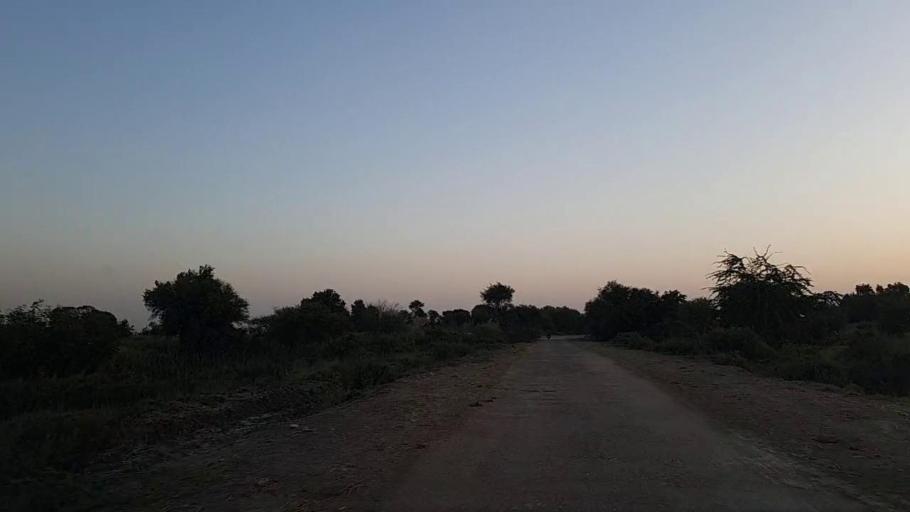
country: PK
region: Sindh
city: Mirpur Batoro
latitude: 24.6189
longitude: 68.1839
